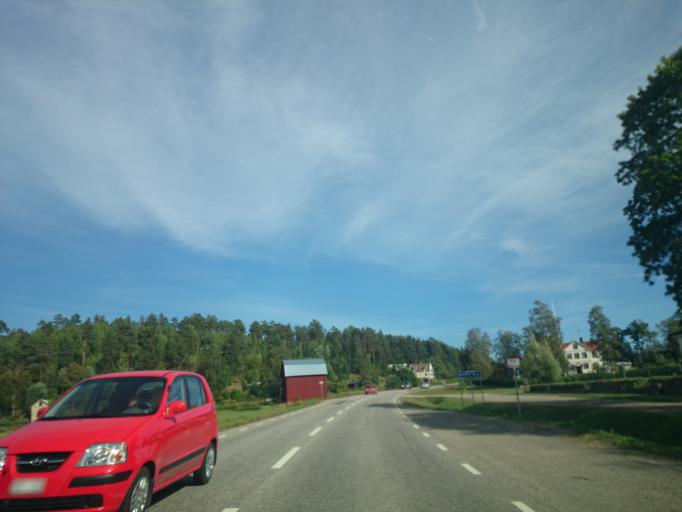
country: SE
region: Gaevleborg
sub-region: Hudiksvalls Kommun
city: Sorforsa
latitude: 61.7666
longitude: 17.0403
